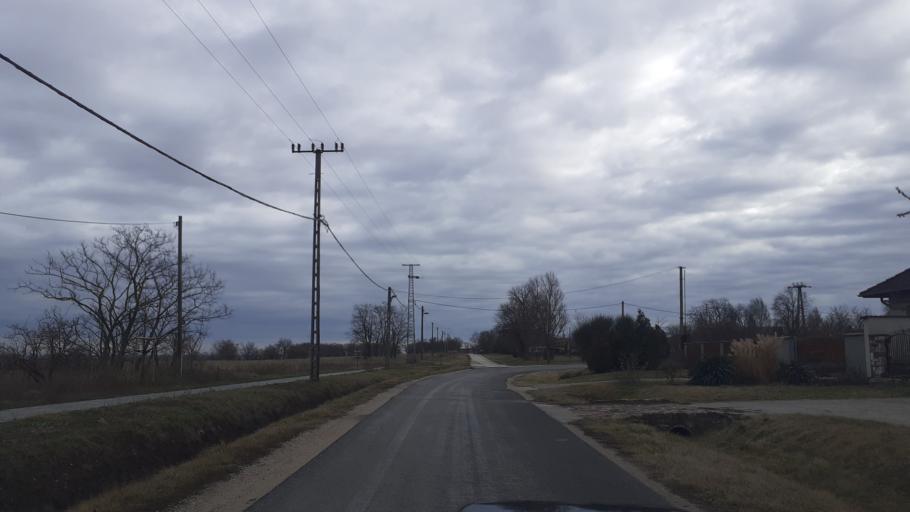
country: HU
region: Fejer
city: Pakozd
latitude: 47.1657
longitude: 18.5223
